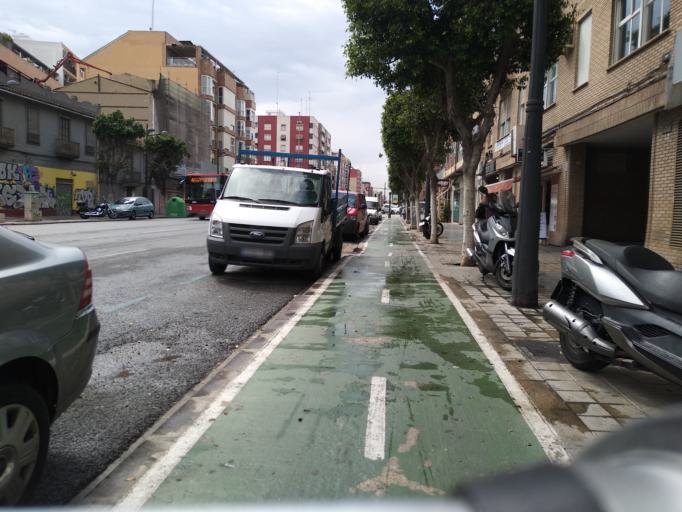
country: ES
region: Valencia
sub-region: Provincia de Valencia
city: Alboraya
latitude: 39.4615
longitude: -0.3374
